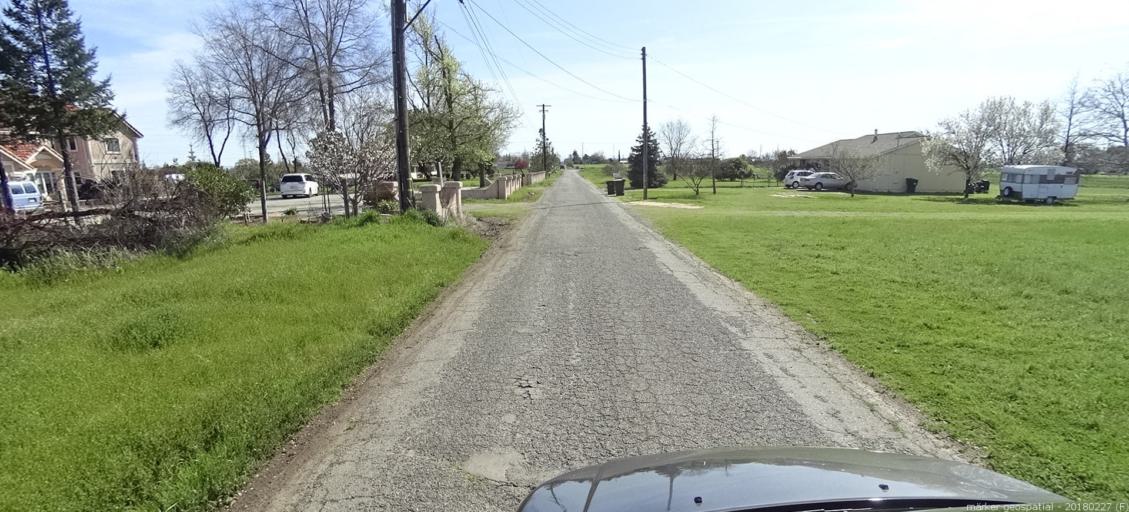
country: US
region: California
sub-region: Sacramento County
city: Rosemont
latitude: 38.5071
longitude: -121.3654
